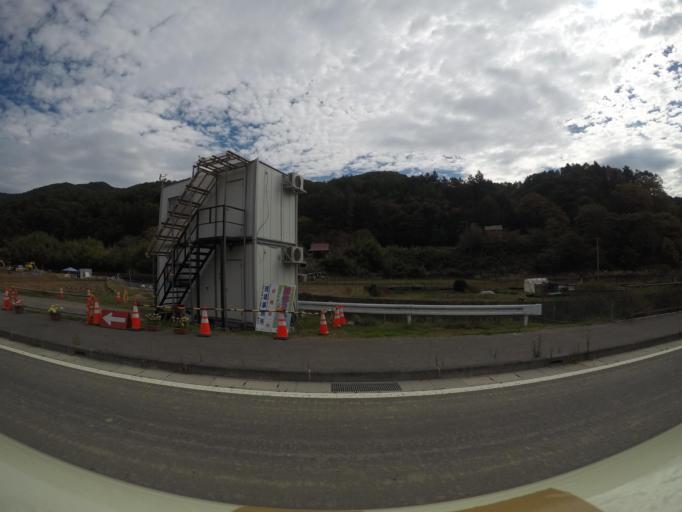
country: JP
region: Nagano
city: Chino
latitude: 35.8913
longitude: 138.0985
